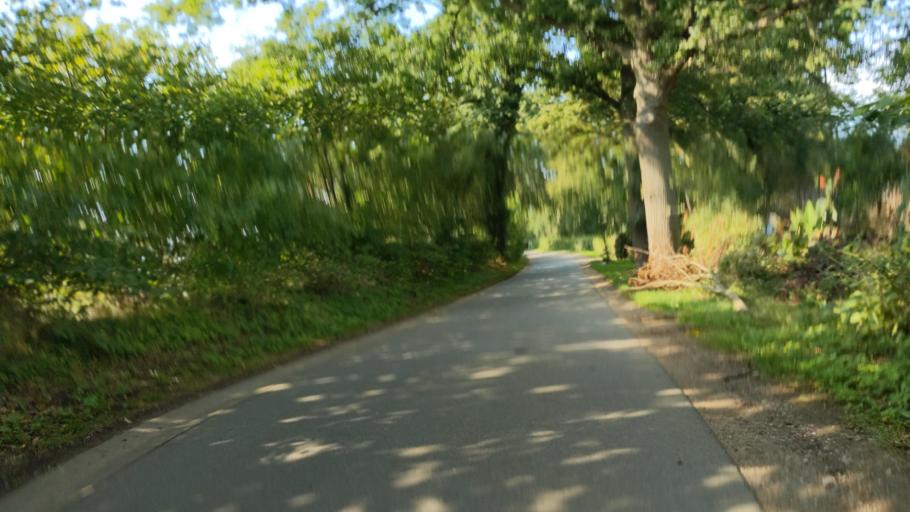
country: DE
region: Mecklenburg-Vorpommern
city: Kalkhorst
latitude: 53.9749
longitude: 11.0099
